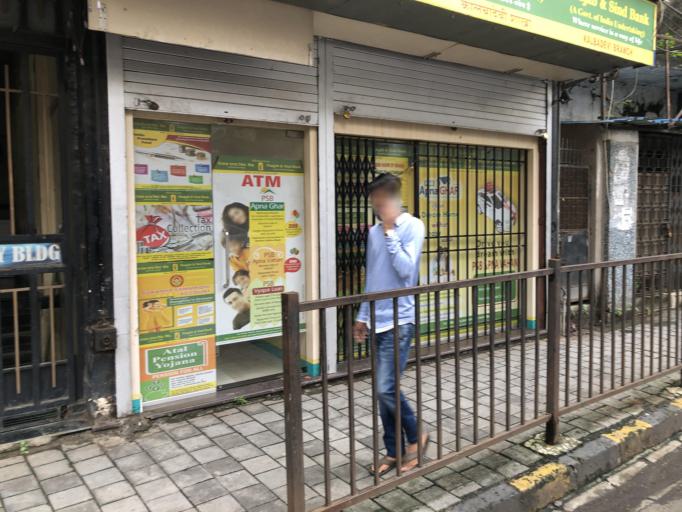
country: IN
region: Maharashtra
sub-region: Raigarh
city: Uran
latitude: 18.9446
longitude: 72.8282
